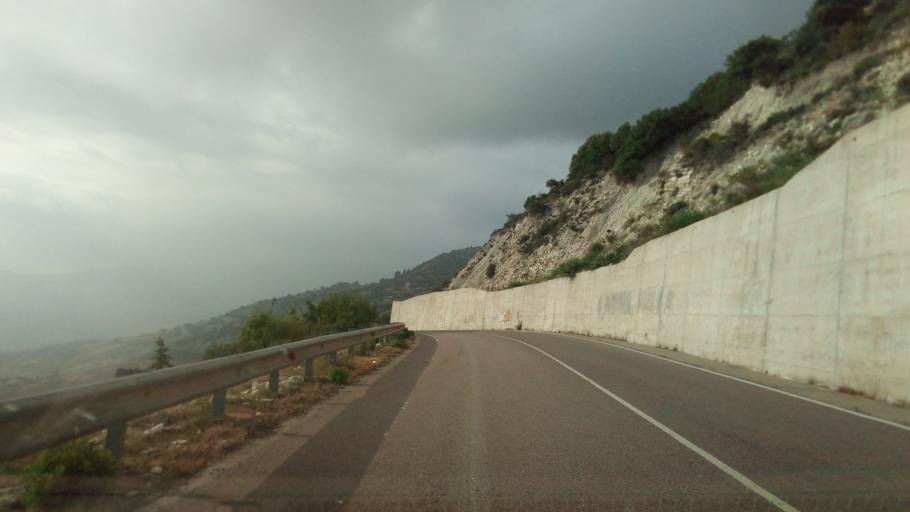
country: CY
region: Limassol
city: Pachna
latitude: 34.8282
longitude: 32.6860
